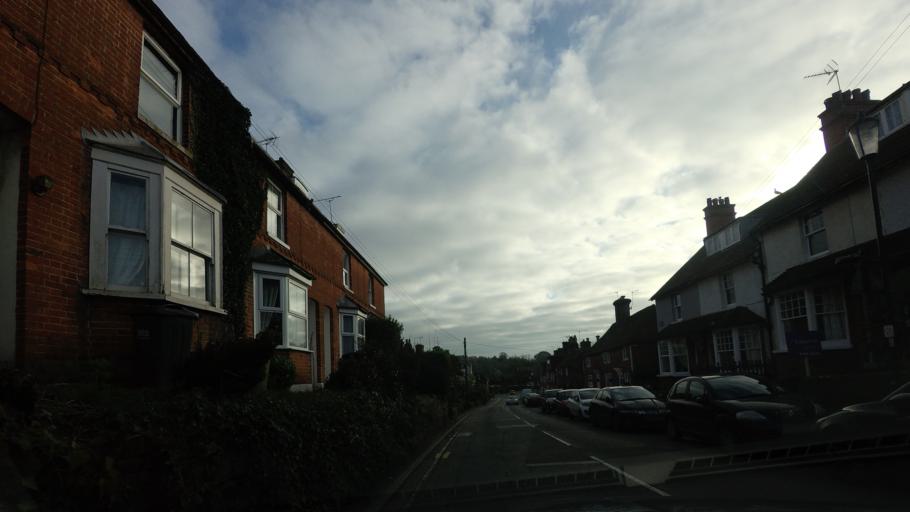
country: GB
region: England
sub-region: East Sussex
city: Battle
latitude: 50.9140
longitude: 0.4910
